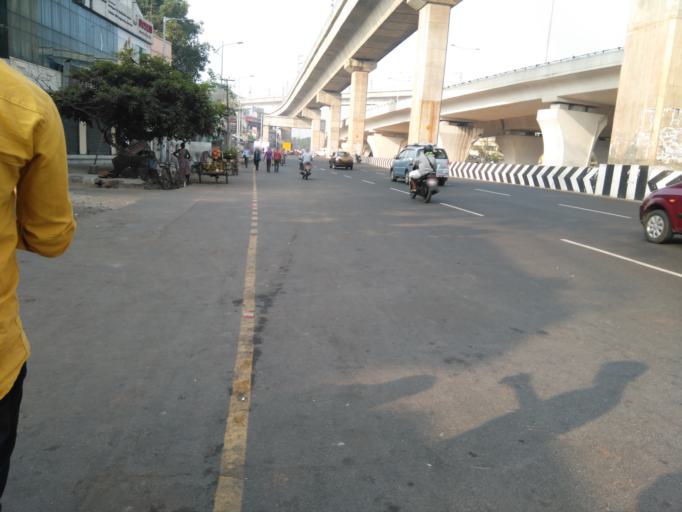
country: IN
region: Tamil Nadu
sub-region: Kancheepuram
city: Alandur
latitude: 13.0065
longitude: 80.2039
